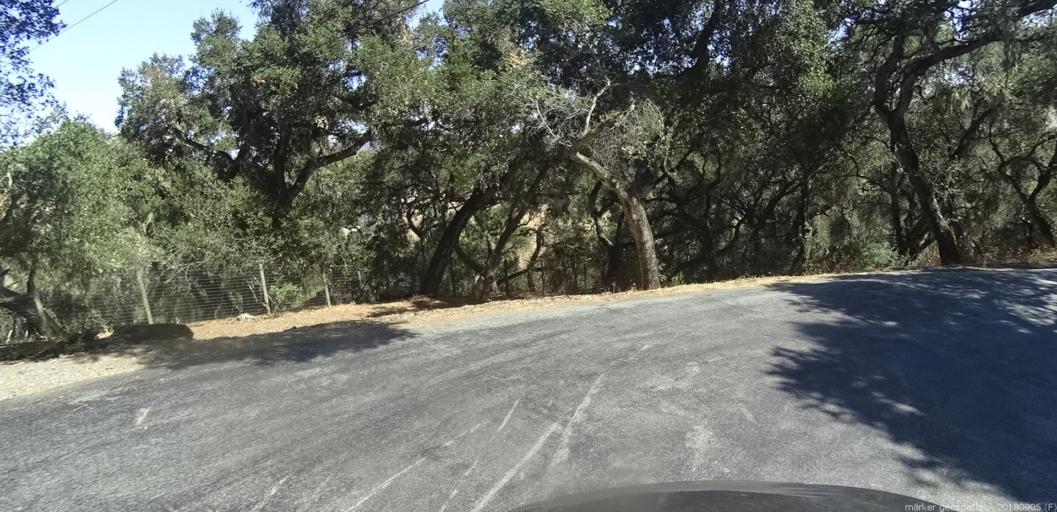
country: US
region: California
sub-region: Monterey County
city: Carmel Valley Village
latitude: 36.4460
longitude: -121.6912
